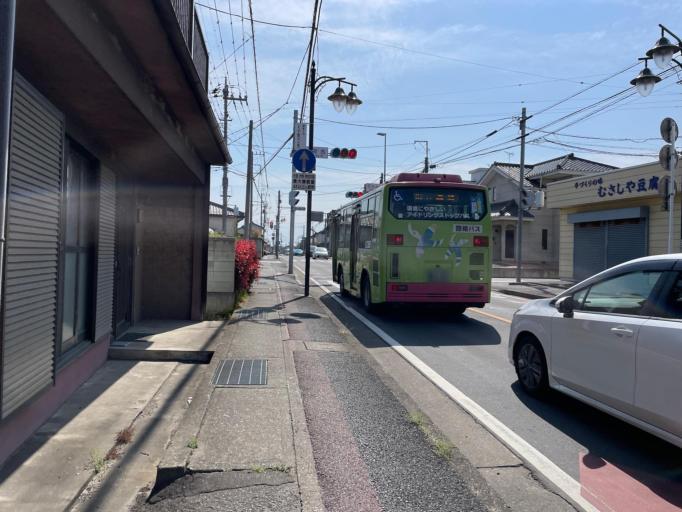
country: JP
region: Gunma
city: Takasaki
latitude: 36.2959
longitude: 139.0515
